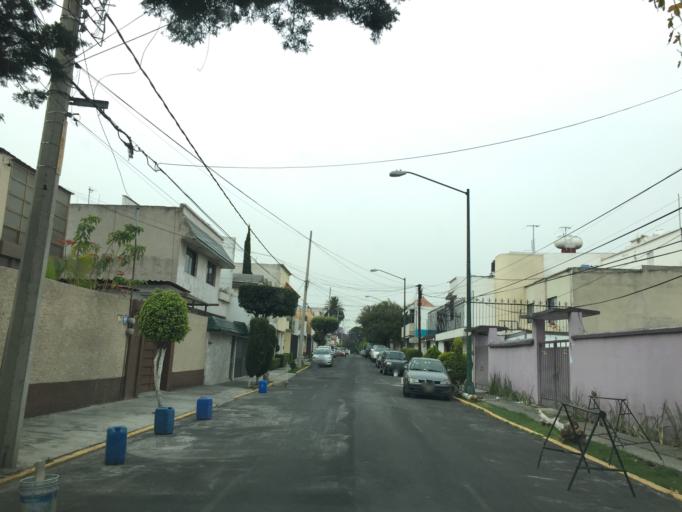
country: MX
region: Mexico
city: Colonia Lindavista
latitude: 19.4980
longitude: -99.1247
